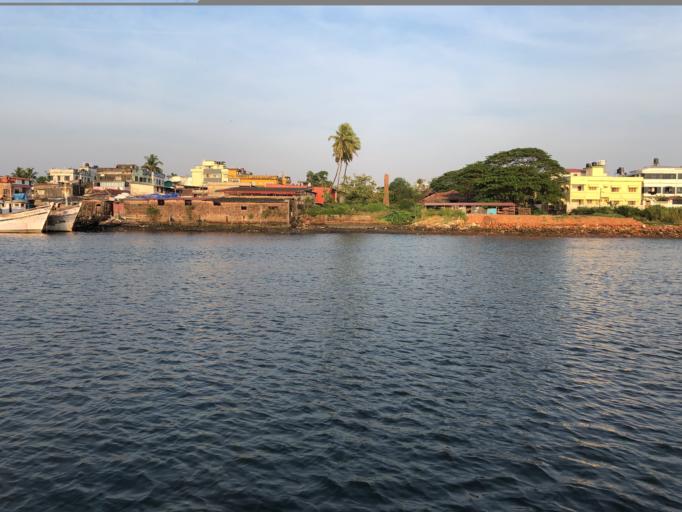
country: IN
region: Karnataka
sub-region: Dakshina Kannada
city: Mangalore
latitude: 12.8736
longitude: 74.8283
